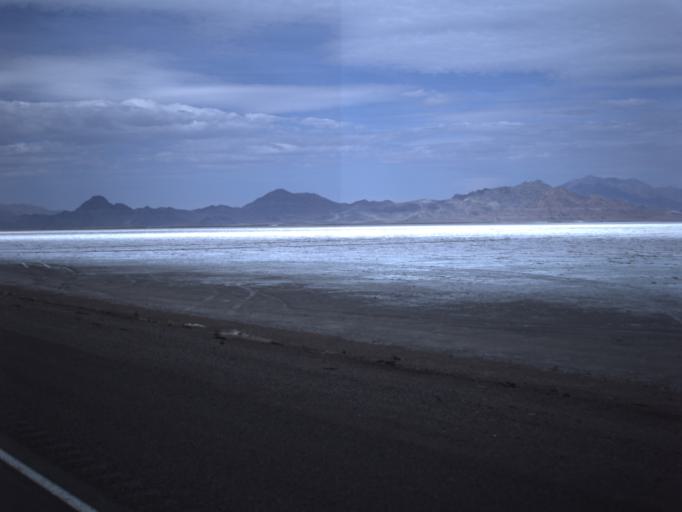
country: US
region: Utah
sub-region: Tooele County
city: Wendover
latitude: 40.7385
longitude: -113.8072
